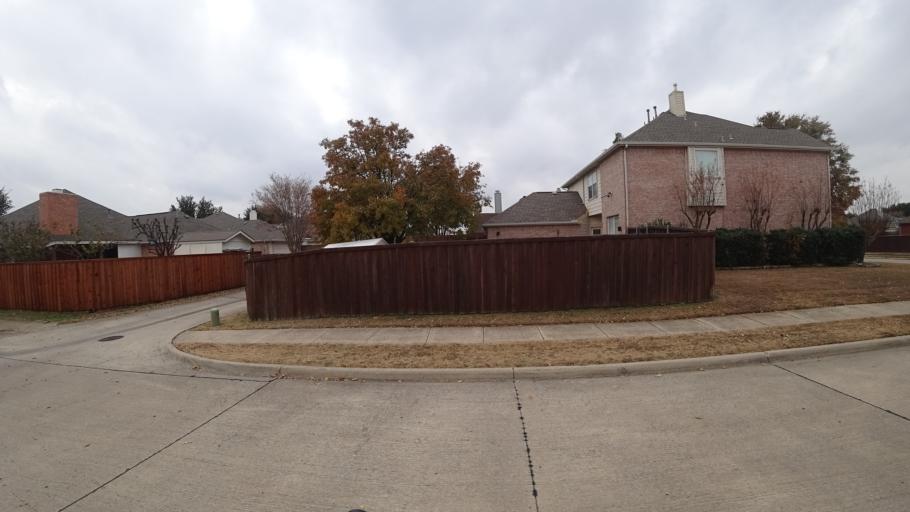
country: US
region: Texas
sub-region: Denton County
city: Lewisville
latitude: 33.0176
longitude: -96.9407
